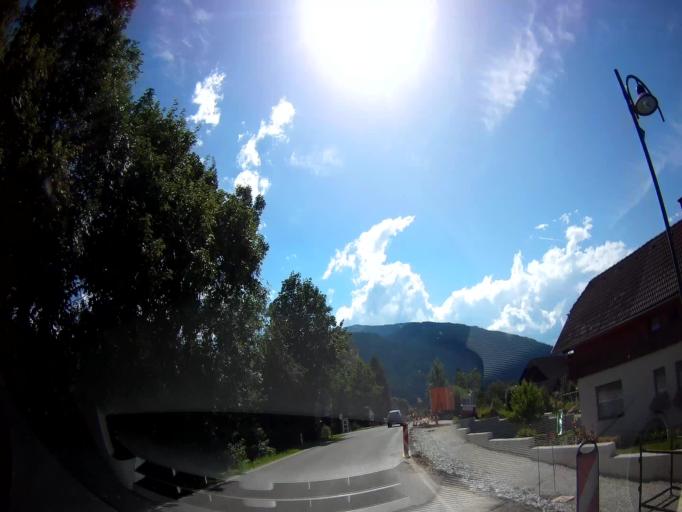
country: AT
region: Salzburg
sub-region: Politischer Bezirk Tamsweg
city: Sankt Margarethen im Lungau
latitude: 47.0823
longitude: 13.7007
